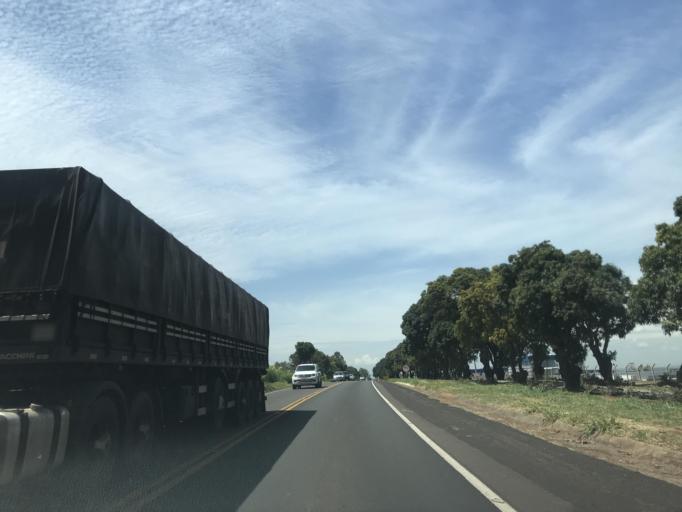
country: BR
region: Parana
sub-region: Paranavai
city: Nova Aurora
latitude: -22.9775
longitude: -52.6057
